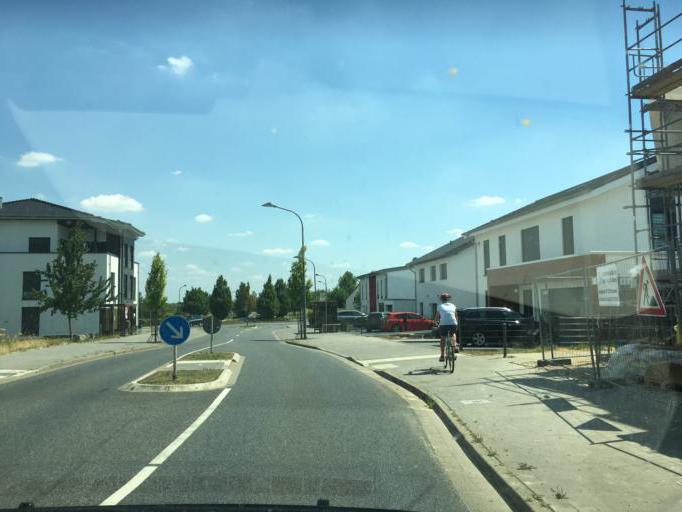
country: DE
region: North Rhine-Westphalia
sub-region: Regierungsbezirk Koln
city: Langerwehe
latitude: 50.8083
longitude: 6.3792
